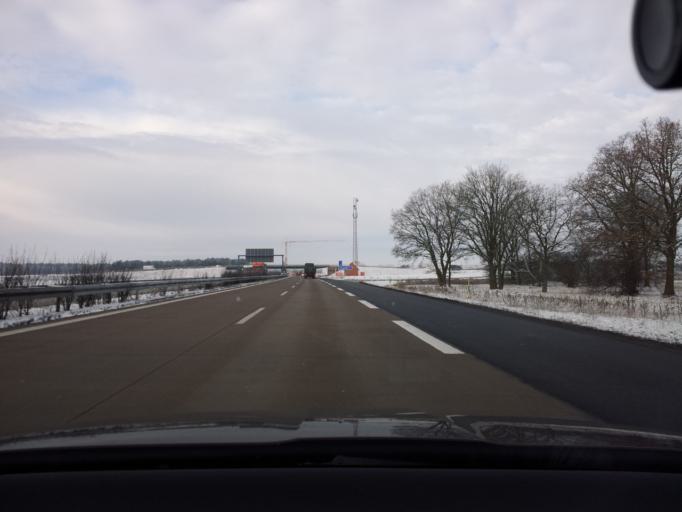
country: DE
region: Mecklenburg-Vorpommern
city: Rastow
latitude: 53.4295
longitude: 11.5001
